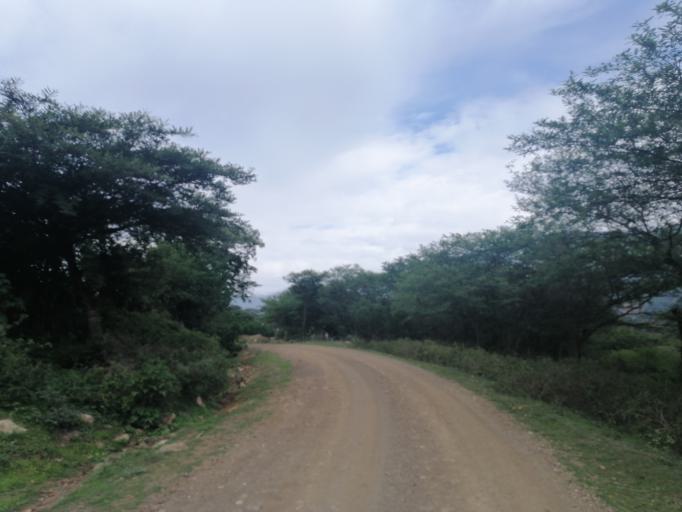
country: EC
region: Loja
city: Catacocha
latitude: -4.0115
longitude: -79.6902
